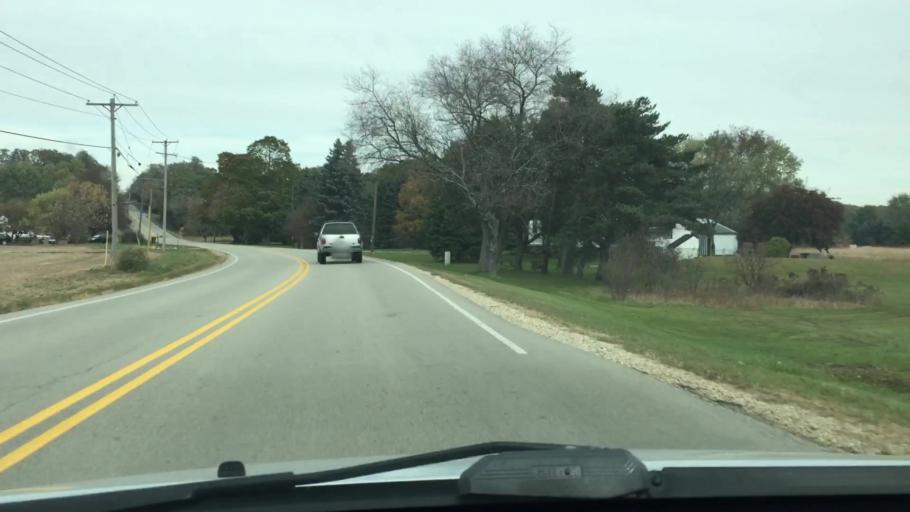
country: US
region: Wisconsin
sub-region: Waukesha County
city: North Prairie
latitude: 42.9192
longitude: -88.4056
